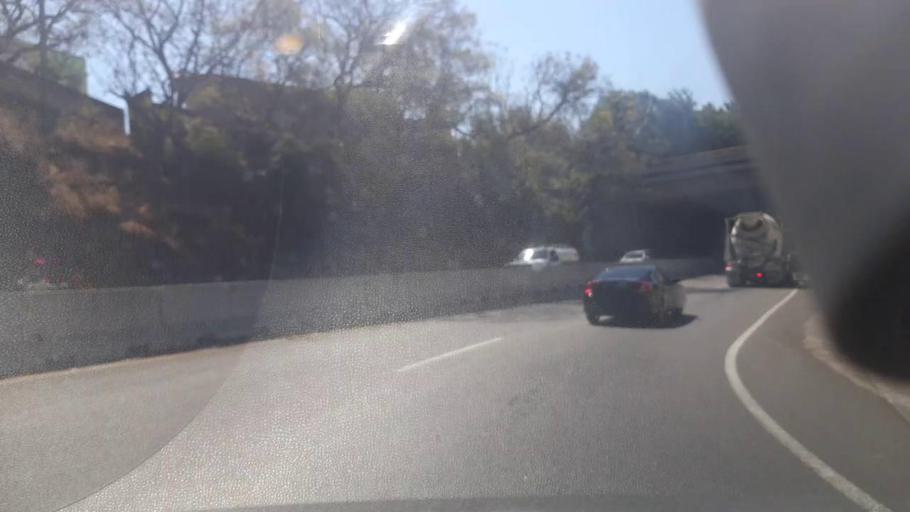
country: MX
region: Morelos
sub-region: Cuernavaca
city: Fraccionamiento Lomas de Ahuatlan
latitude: 18.9698
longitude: -99.2378
